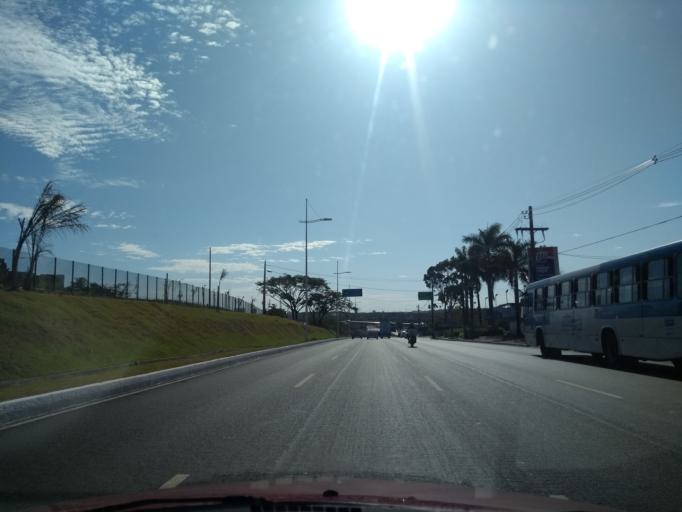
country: BR
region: Bahia
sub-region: Lauro De Freitas
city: Lauro de Freitas
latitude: -12.9244
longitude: -38.3759
